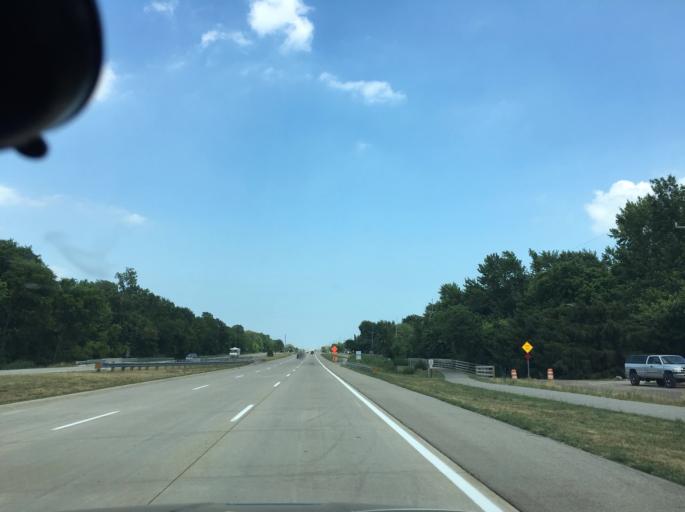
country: US
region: Michigan
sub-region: Macomb County
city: Clinton
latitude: 42.5686
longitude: -82.9299
